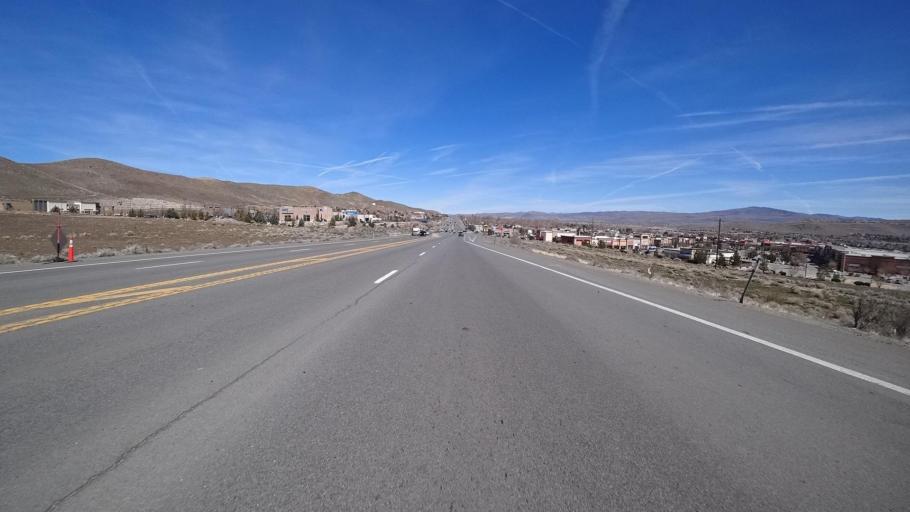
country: US
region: Nevada
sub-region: Washoe County
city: Sun Valley
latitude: 39.5802
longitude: -119.7446
